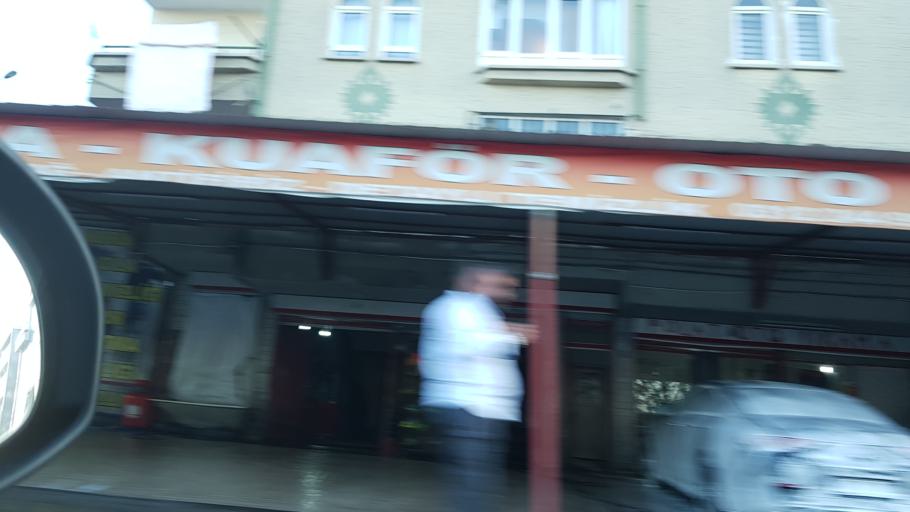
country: TR
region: Ankara
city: Etimesgut
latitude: 39.9475
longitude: 32.6701
